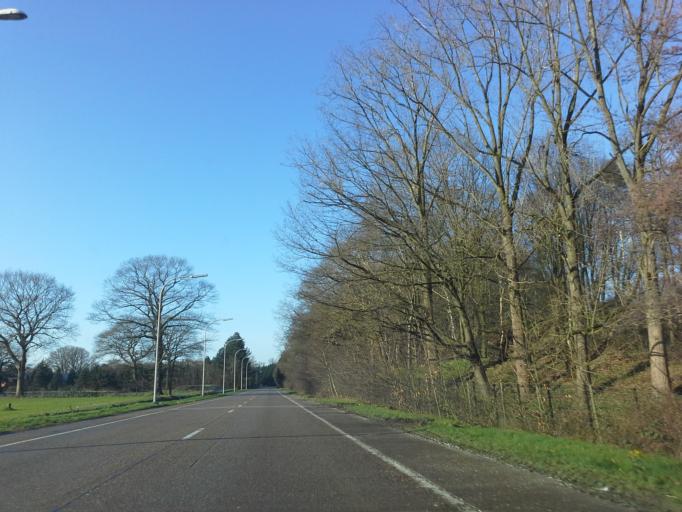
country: BE
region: Flanders
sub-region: Provincie Antwerpen
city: Olen
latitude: 51.1578
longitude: 4.8566
